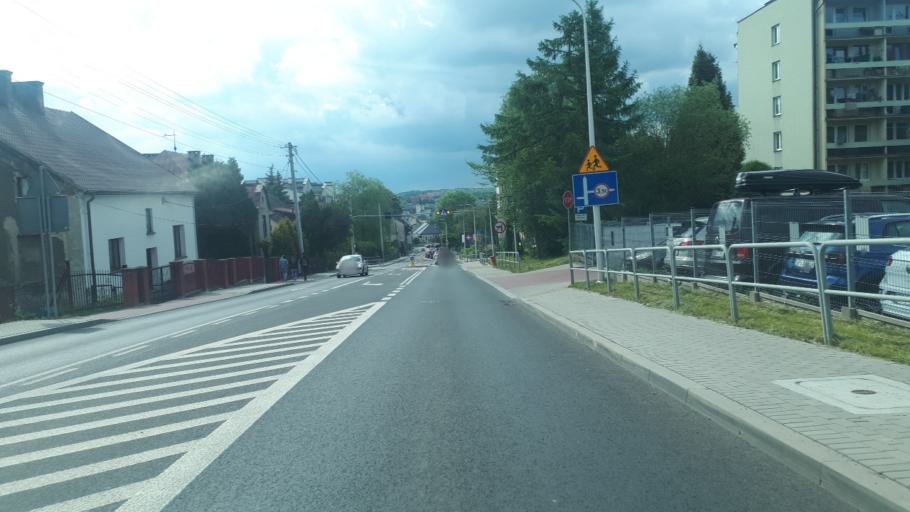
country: PL
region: Silesian Voivodeship
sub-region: Bielsko-Biala
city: Bielsko-Biala
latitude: 49.8210
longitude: 19.0633
